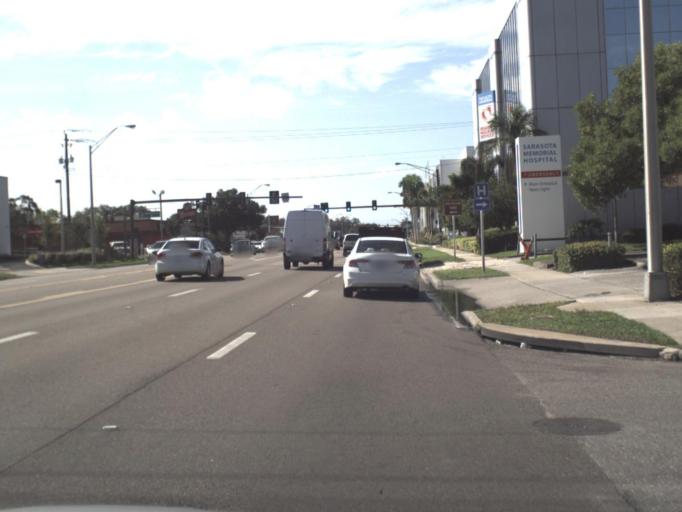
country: US
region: Florida
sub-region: Sarasota County
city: Sarasota
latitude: 27.3202
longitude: -82.5298
